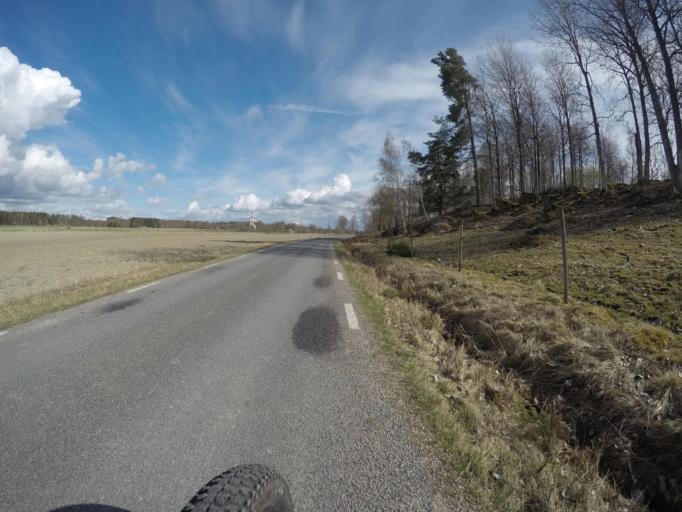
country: SE
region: Vaestmanland
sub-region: Kungsors Kommun
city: Kungsoer
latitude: 59.2877
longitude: 16.1488
